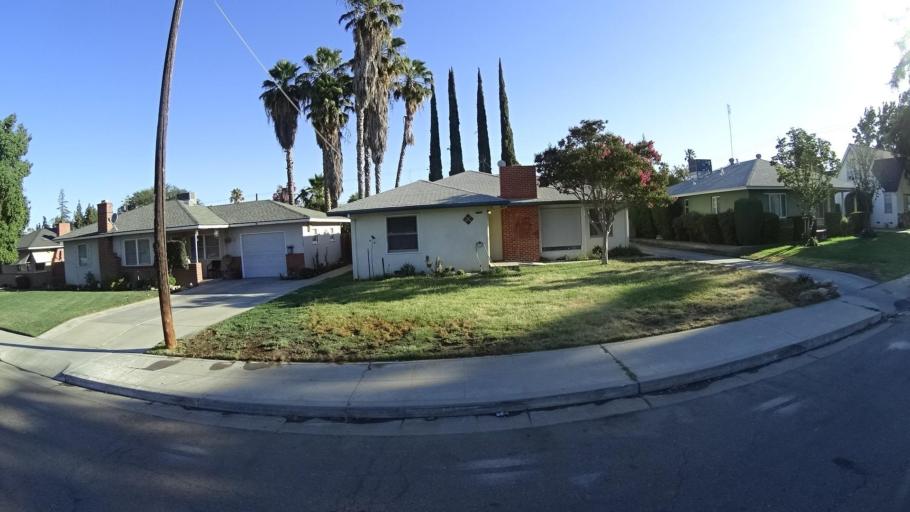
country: US
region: California
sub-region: Fresno County
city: Fresno
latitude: 36.7702
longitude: -119.8229
